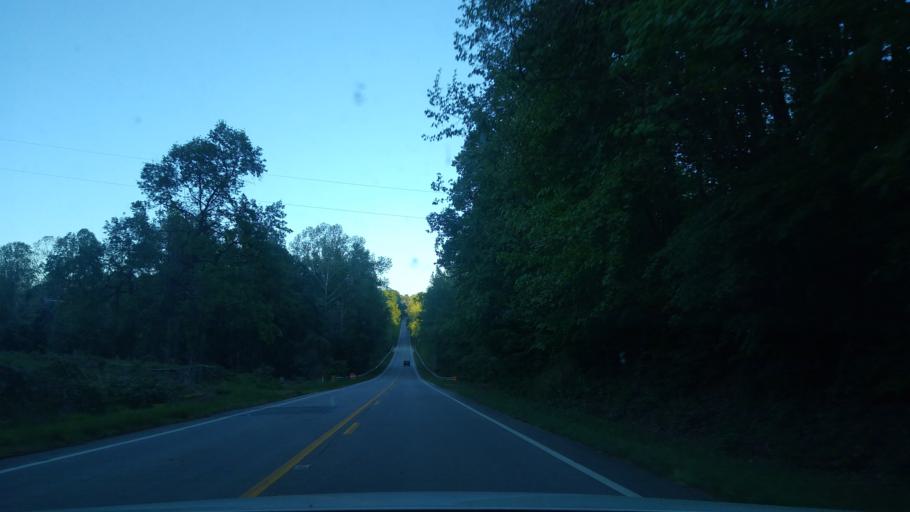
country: US
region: North Carolina
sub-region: Rockingham County
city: Reidsville
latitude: 36.3983
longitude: -79.5335
